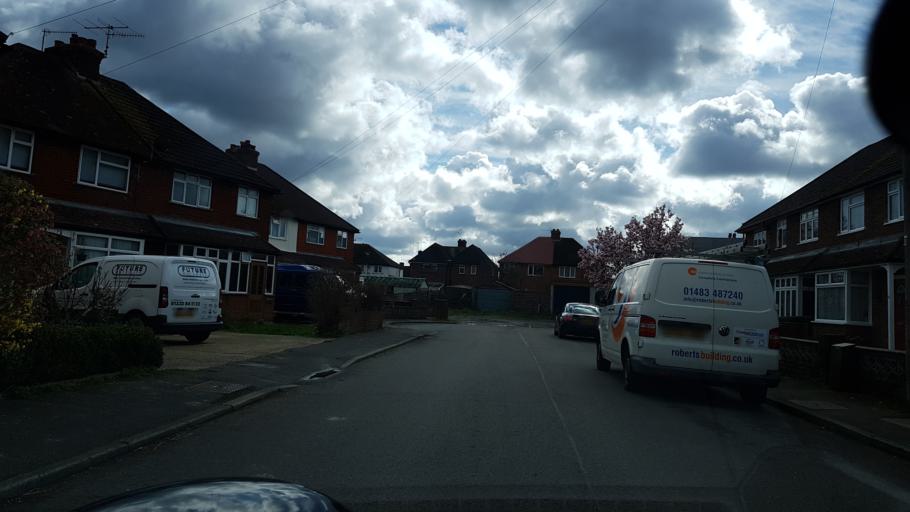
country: GB
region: England
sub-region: Surrey
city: Guildford
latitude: 51.2591
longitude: -0.5706
